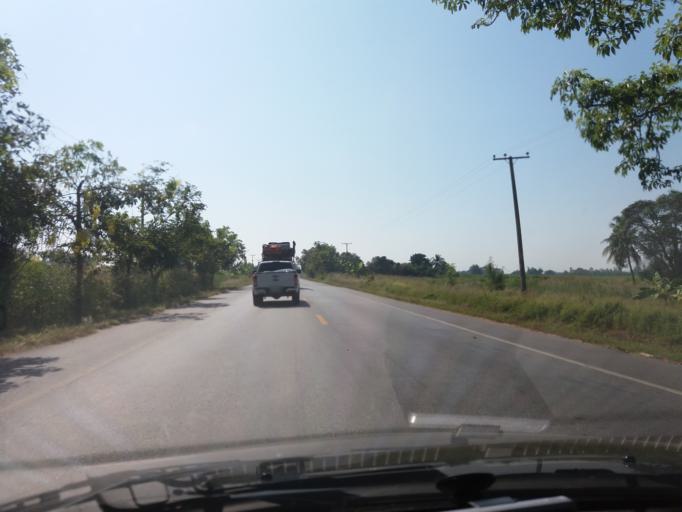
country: TH
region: Kamphaeng Phet
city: Khanu Woralaksaburi
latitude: 16.1419
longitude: 99.8136
